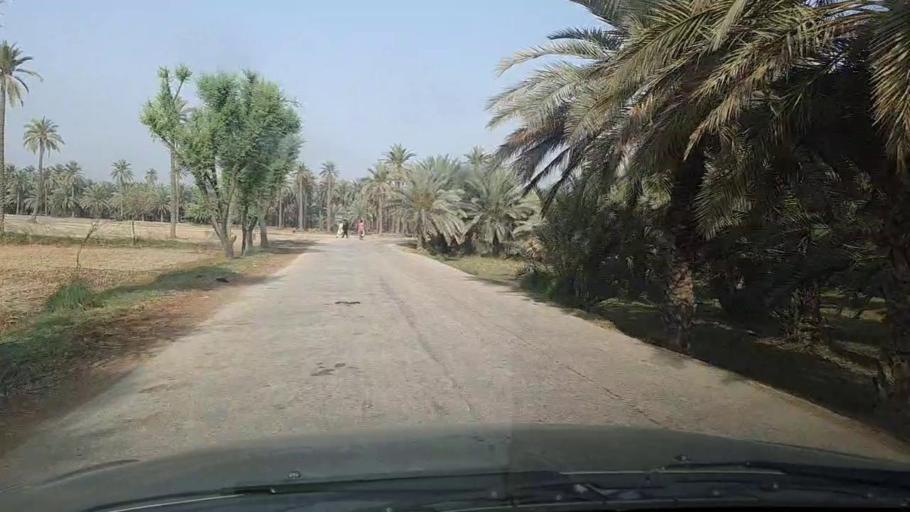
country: PK
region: Sindh
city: Pir jo Goth
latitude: 27.5609
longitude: 68.5522
